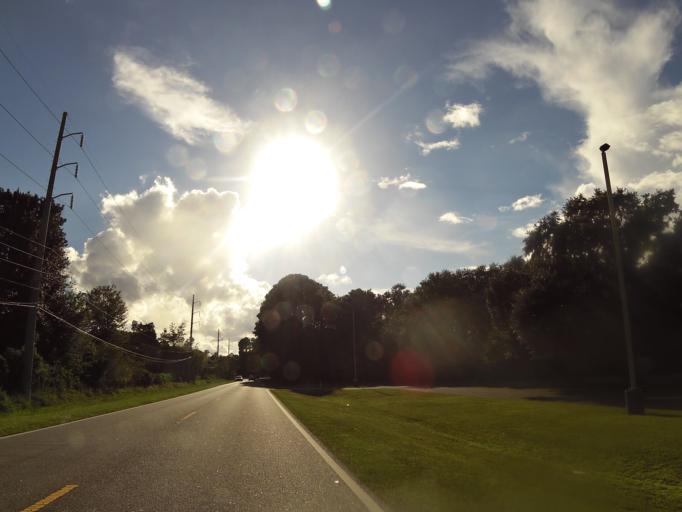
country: US
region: Georgia
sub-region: Glynn County
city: Country Club Estates
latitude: 31.2262
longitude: -81.4728
